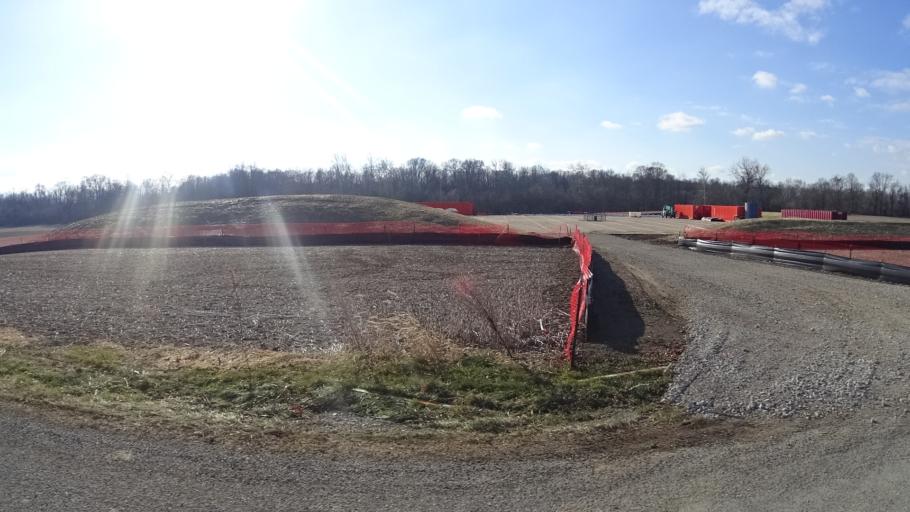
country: US
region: Ohio
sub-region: Lorain County
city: Wellington
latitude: 41.2236
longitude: -82.2044
